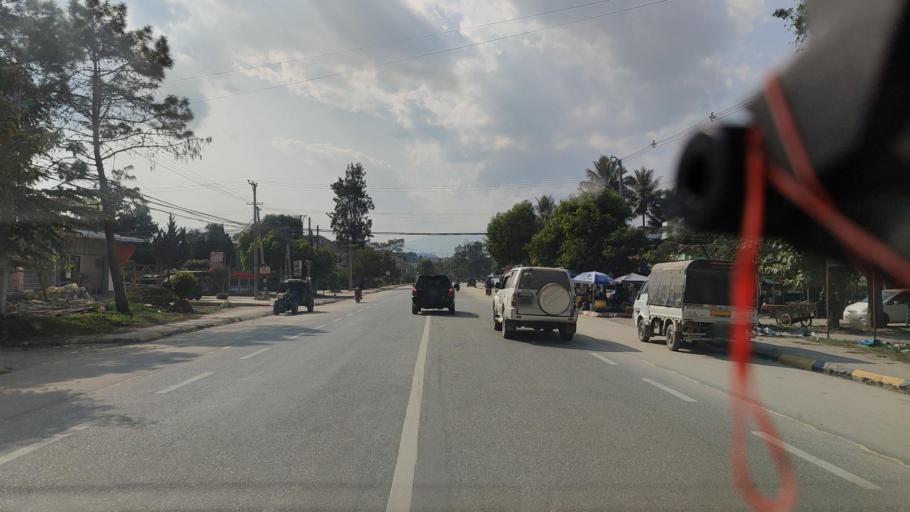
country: TH
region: Chiang Rai
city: Mae Sai
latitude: 21.2985
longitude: 99.6170
